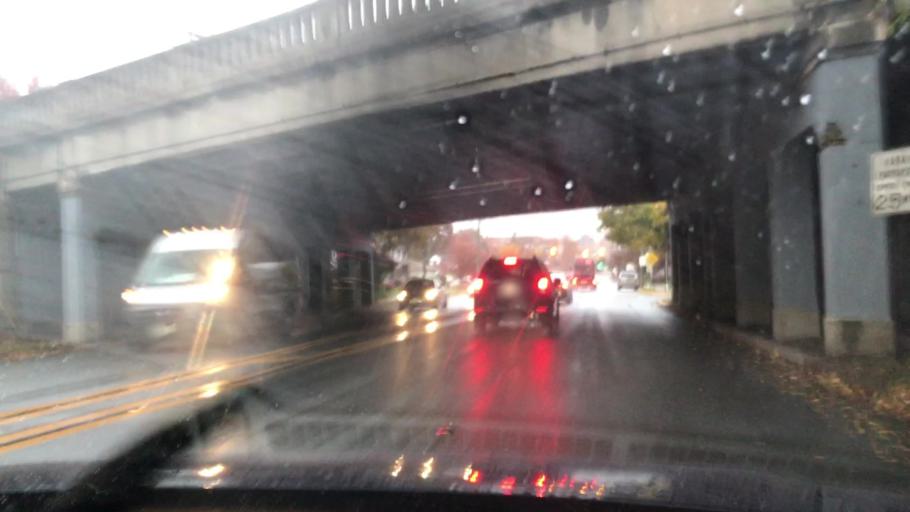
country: US
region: New Jersey
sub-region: Bergen County
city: Lodi
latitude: 40.8721
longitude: -74.0682
